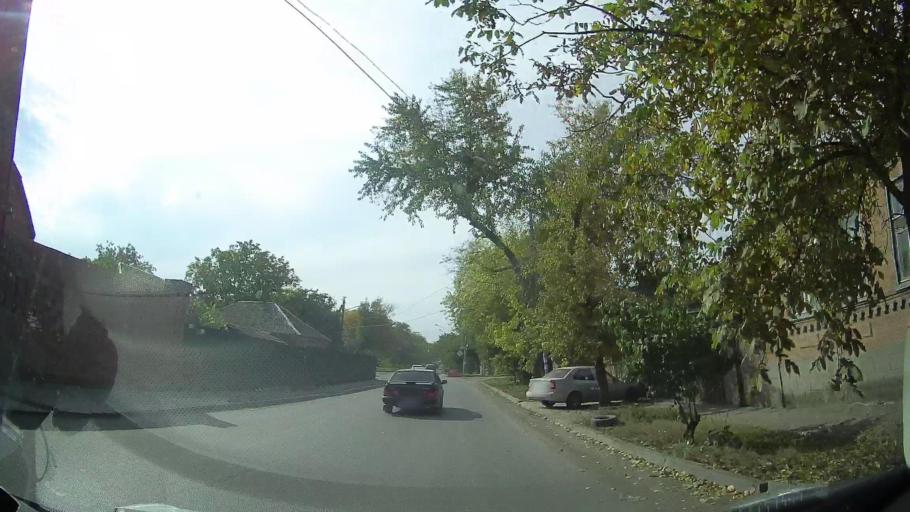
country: RU
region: Rostov
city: Severnyy
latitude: 47.2613
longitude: 39.7060
